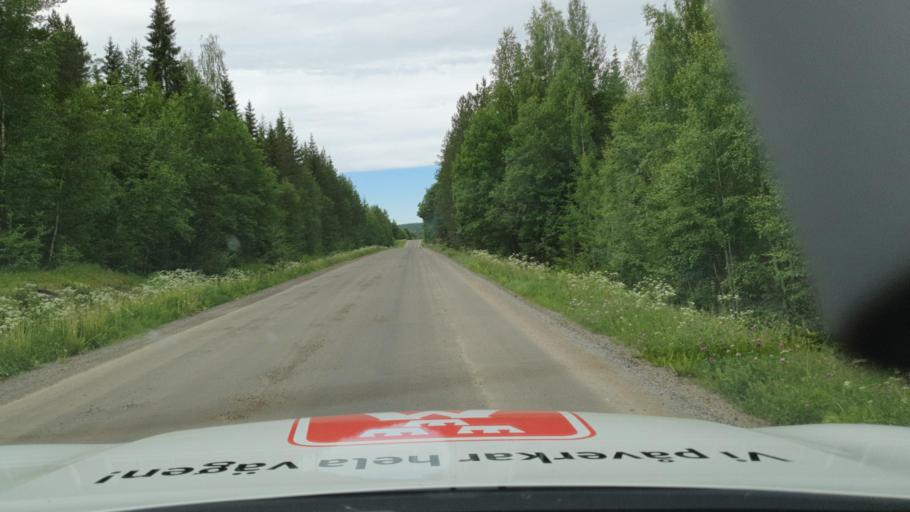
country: SE
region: Vaesterbotten
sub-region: Skelleftea Kommun
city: Burtraesk
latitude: 64.3586
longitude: 20.4395
